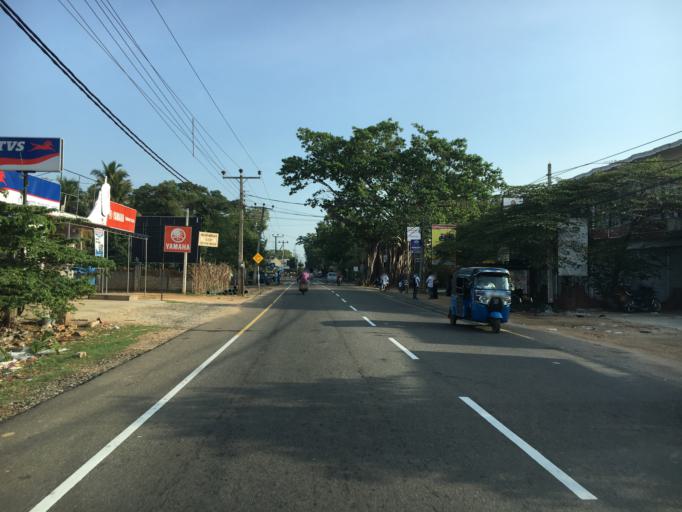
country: LK
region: Eastern Province
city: Eravur Town
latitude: 7.9065
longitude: 81.5342
